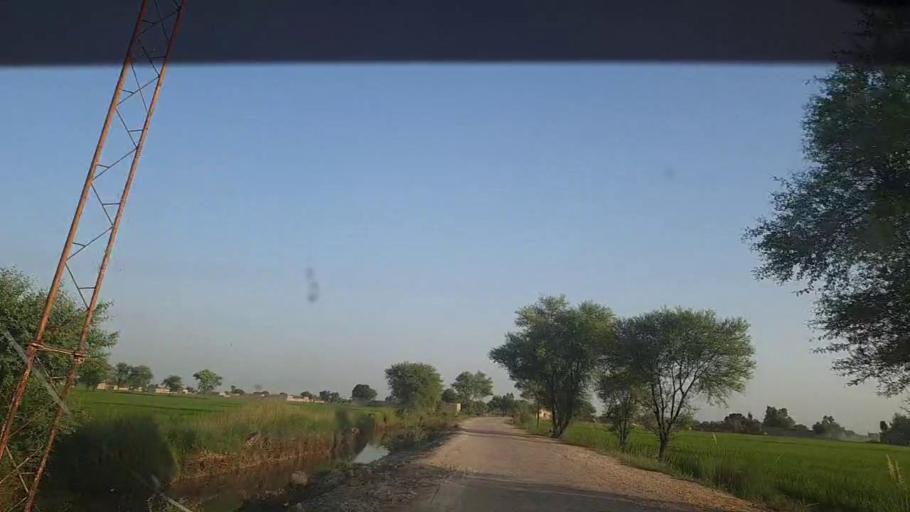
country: PK
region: Sindh
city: Thul
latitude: 28.1224
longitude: 68.8947
